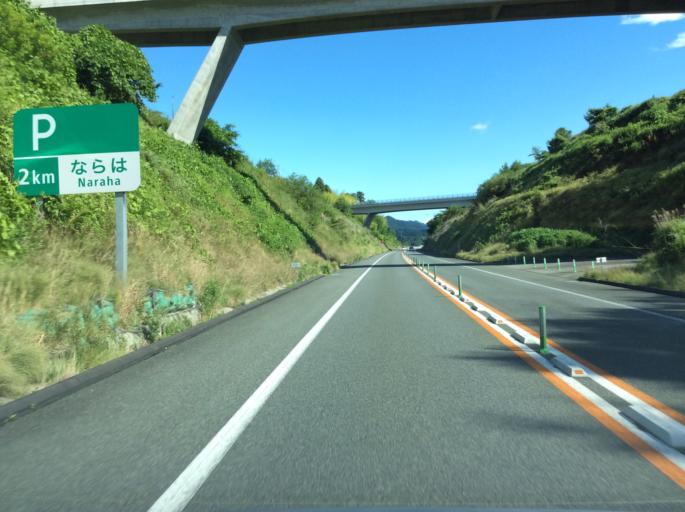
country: JP
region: Fukushima
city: Namie
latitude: 37.2679
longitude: 140.9862
